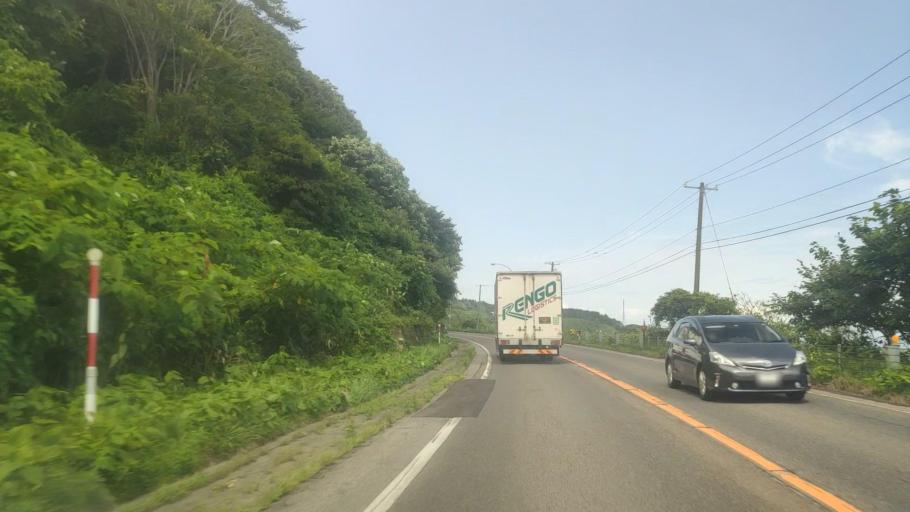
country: JP
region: Hokkaido
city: Nanae
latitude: 42.1630
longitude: 140.4687
